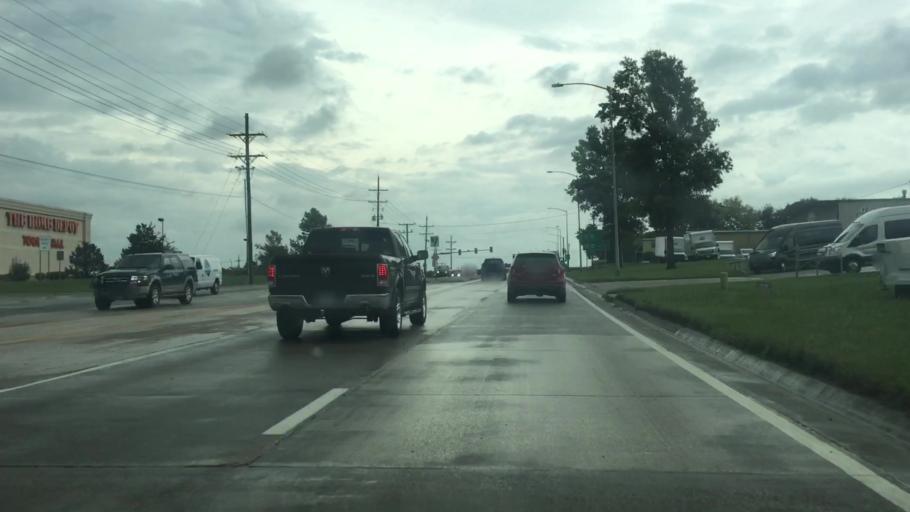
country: US
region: Kansas
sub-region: Johnson County
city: Olathe
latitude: 38.8478
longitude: -94.8158
